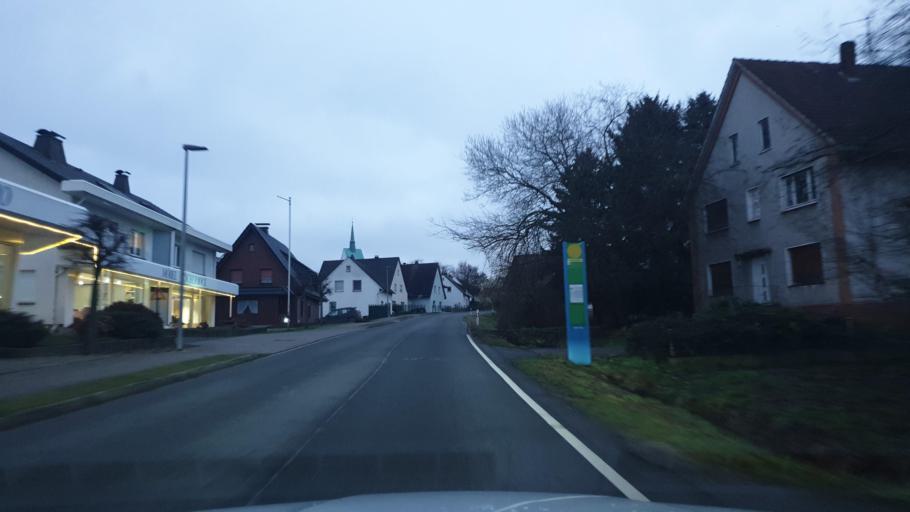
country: DE
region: North Rhine-Westphalia
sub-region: Regierungsbezirk Detmold
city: Vlotho
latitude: 52.1630
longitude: 8.8285
